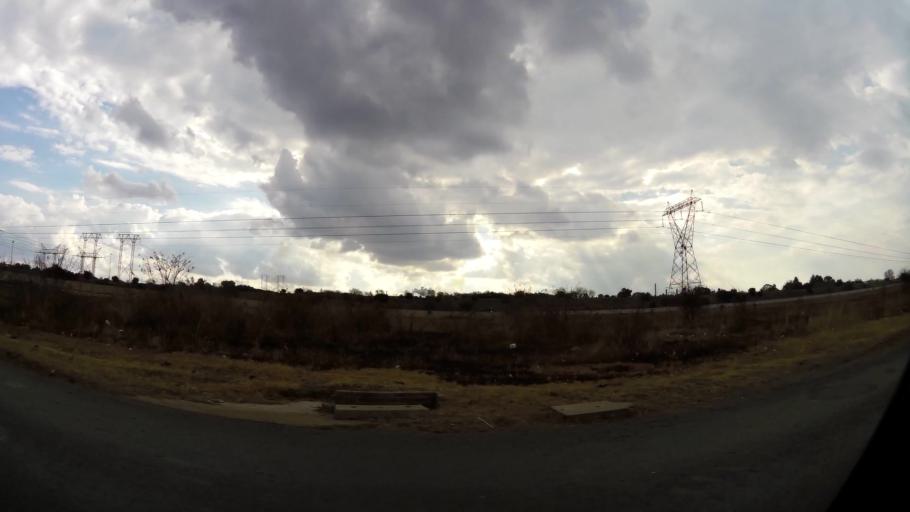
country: ZA
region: Gauteng
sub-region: Sedibeng District Municipality
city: Vanderbijlpark
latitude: -26.6669
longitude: 27.8395
